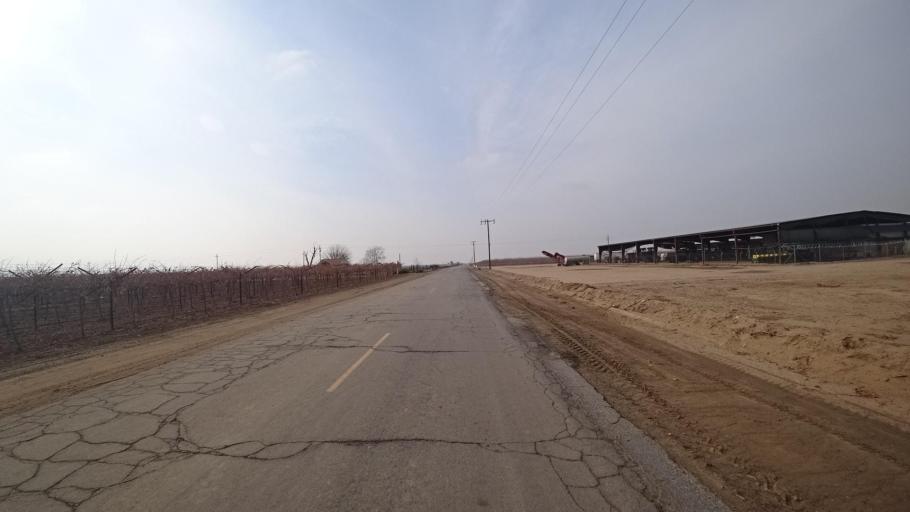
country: US
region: California
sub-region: Kern County
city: Weedpatch
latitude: 35.1364
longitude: -118.9306
